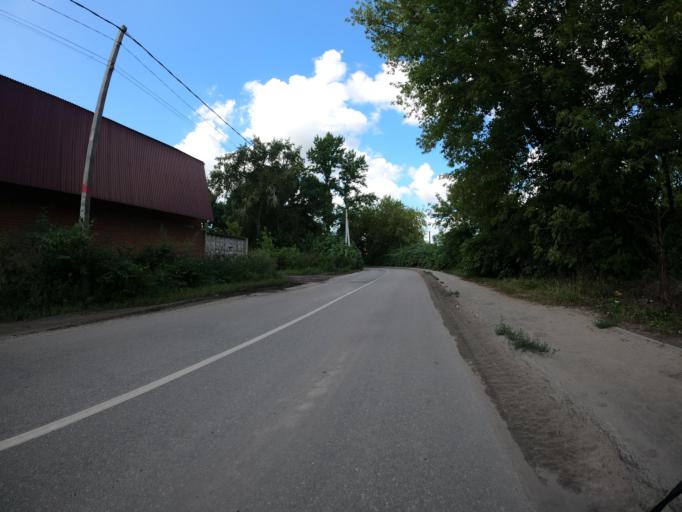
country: RU
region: Moskovskaya
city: Lopatinskiy
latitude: 55.3131
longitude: 38.6966
